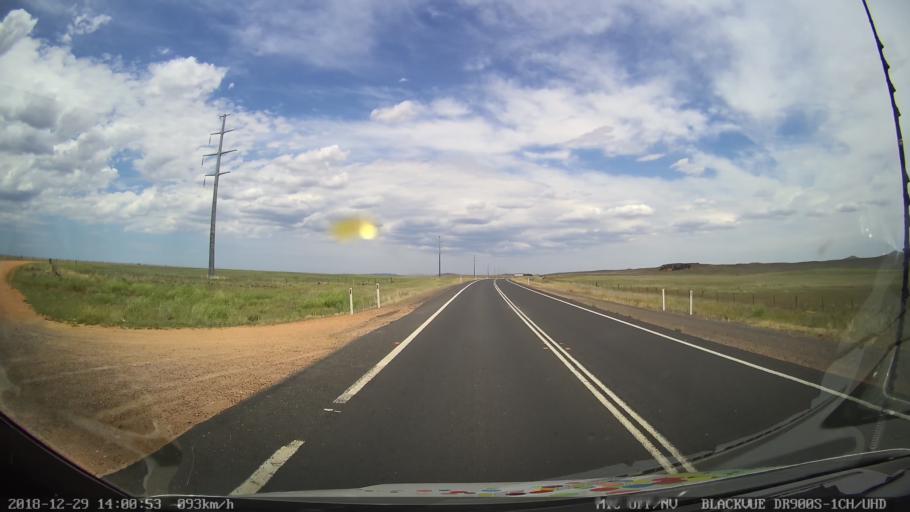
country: AU
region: New South Wales
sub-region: Cooma-Monaro
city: Cooma
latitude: -36.2683
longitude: 149.1641
